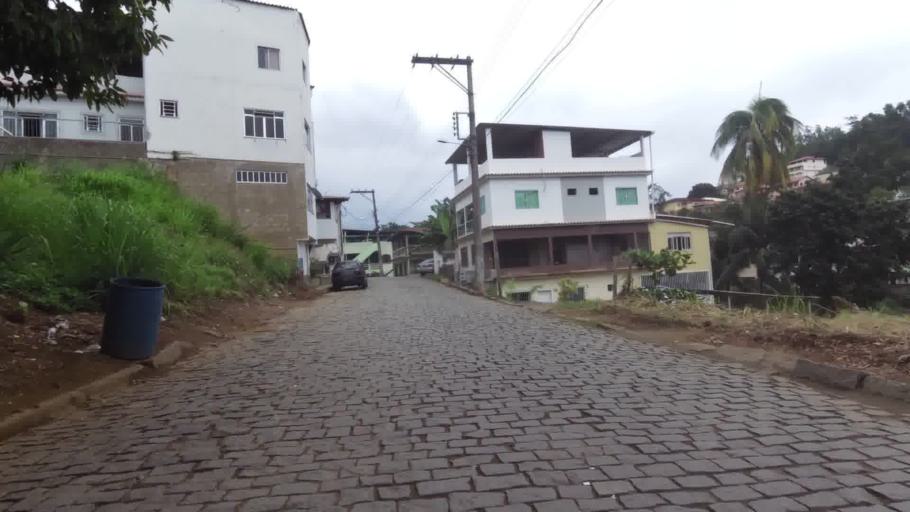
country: BR
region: Espirito Santo
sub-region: Iconha
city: Iconha
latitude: -20.7909
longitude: -40.8137
